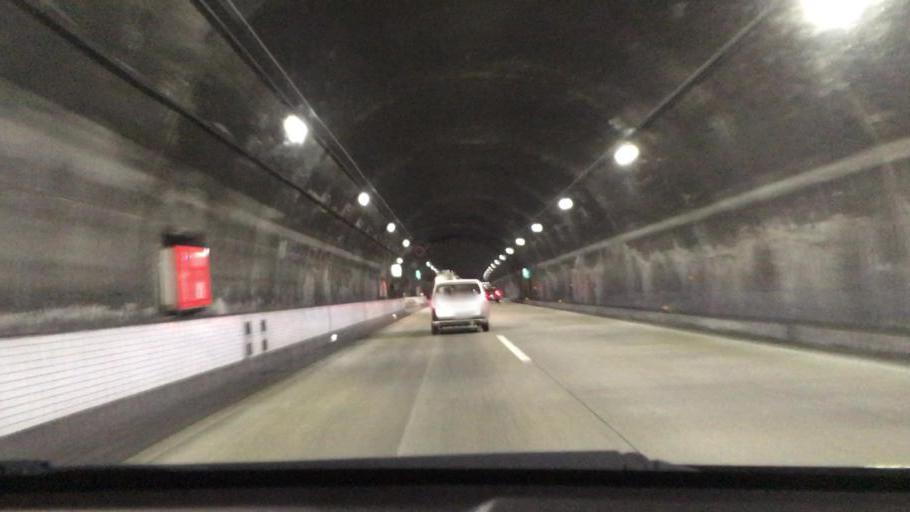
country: JP
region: Yamaguchi
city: Tokuyama
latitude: 34.0719
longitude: 131.7105
